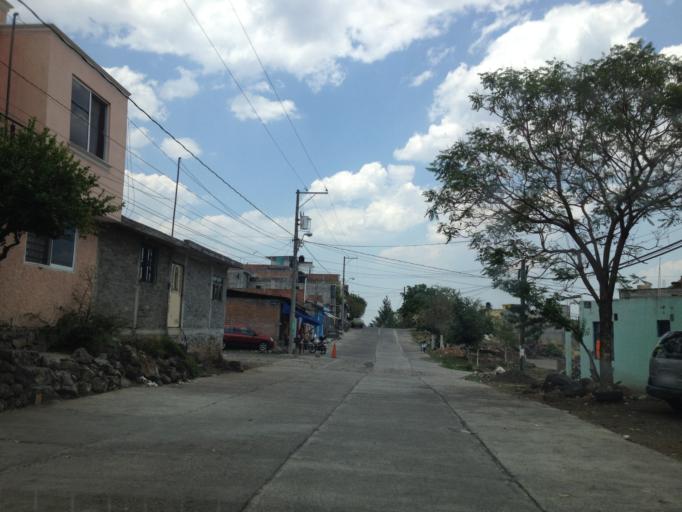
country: MX
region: Michoacan
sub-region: Morelia
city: San Antonio
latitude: 19.7082
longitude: -101.2450
